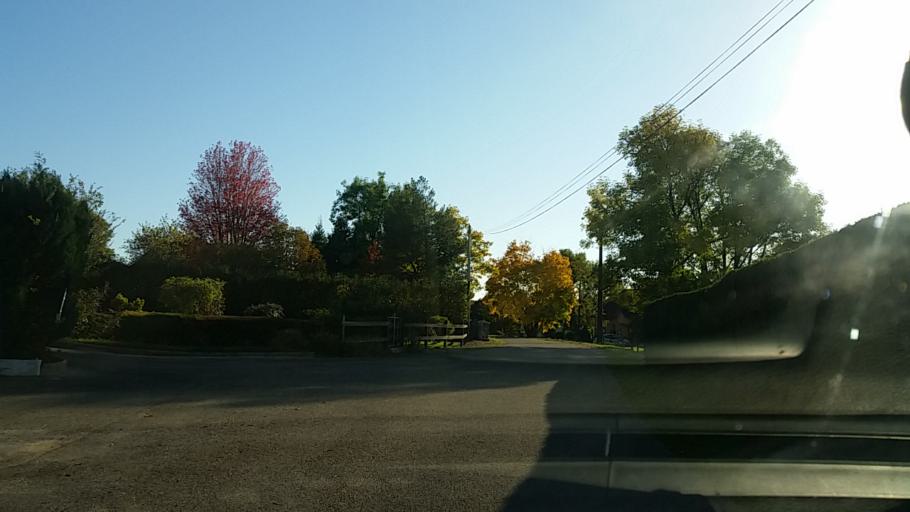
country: FR
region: Franche-Comte
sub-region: Departement du Doubs
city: Ornans
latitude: 47.0407
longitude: 6.0744
